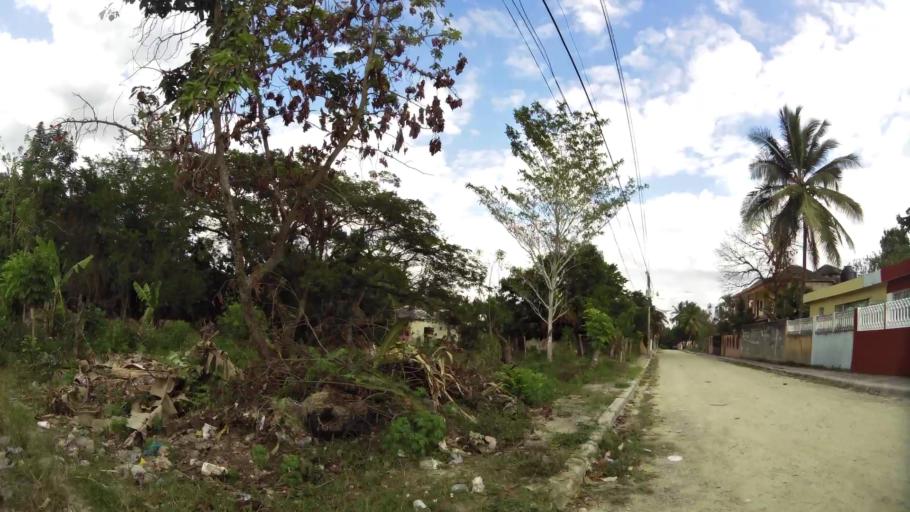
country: DO
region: Nacional
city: Ensanche Luperon
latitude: 18.5598
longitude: -69.9010
